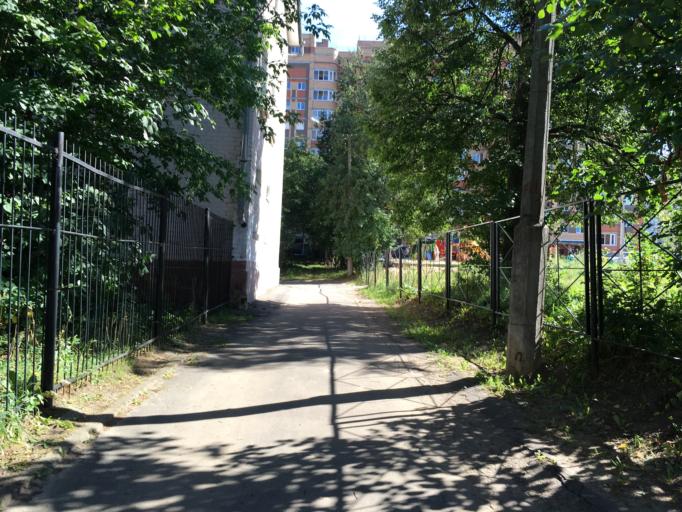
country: RU
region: Mariy-El
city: Yoshkar-Ola
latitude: 56.6437
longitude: 47.8663
